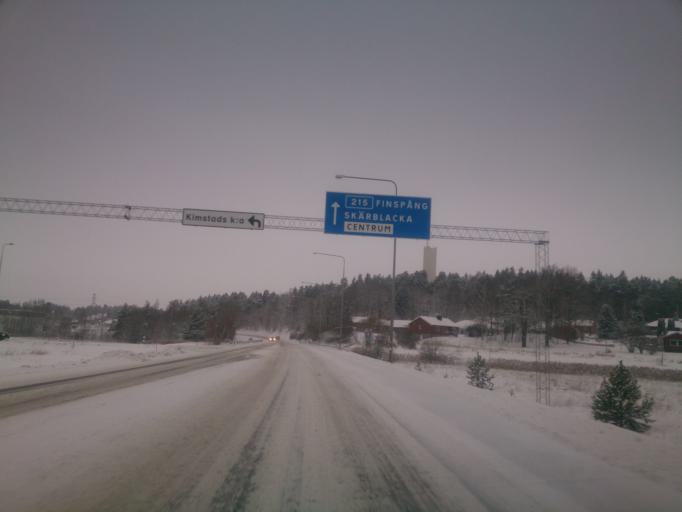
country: SE
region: OEstergoetland
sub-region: Norrkopings Kommun
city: Kimstad
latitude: 58.5415
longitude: 15.9765
